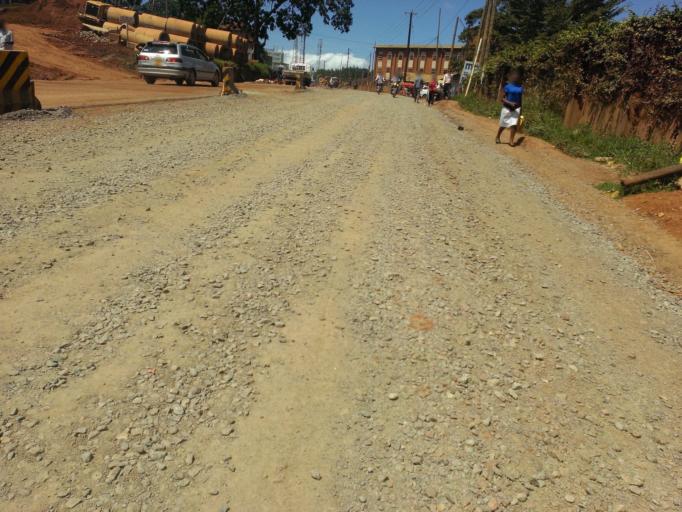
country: UG
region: Central Region
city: Kampala Central Division
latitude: 0.3277
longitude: 32.5659
